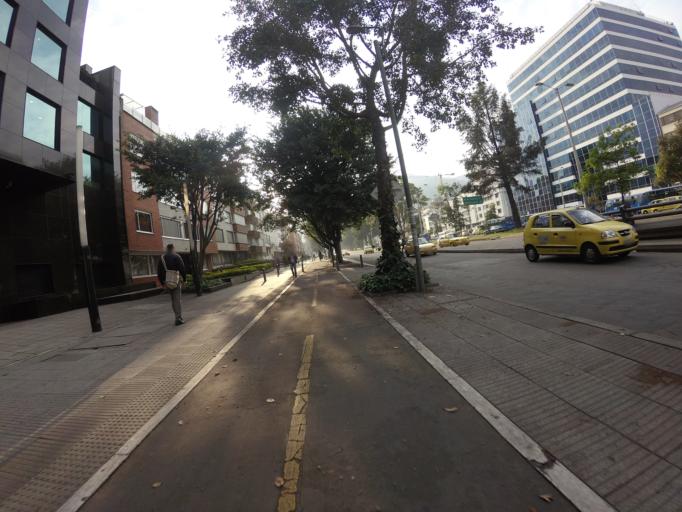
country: CO
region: Bogota D.C.
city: Barrio San Luis
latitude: 4.6844
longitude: -74.0464
